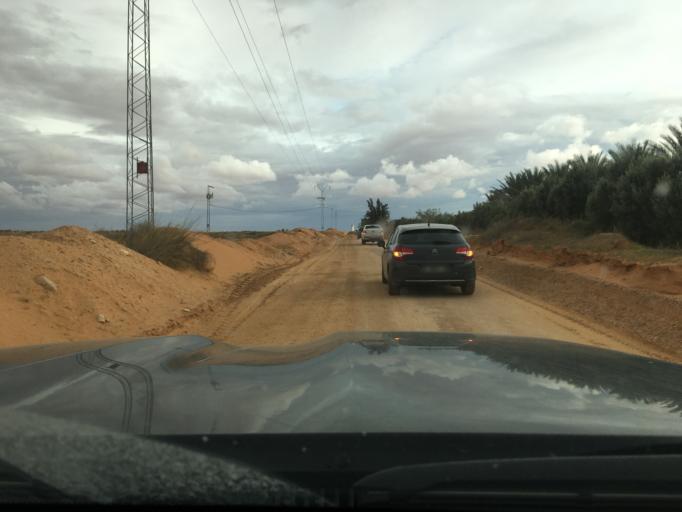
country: TN
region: Madanin
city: Medenine
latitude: 33.2750
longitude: 10.5624
